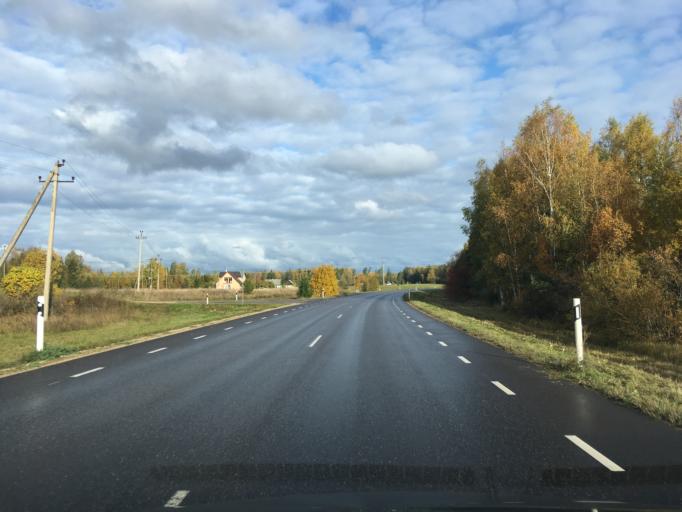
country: EE
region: Harju
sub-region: Raasiku vald
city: Raasiku
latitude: 59.2011
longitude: 25.1833
